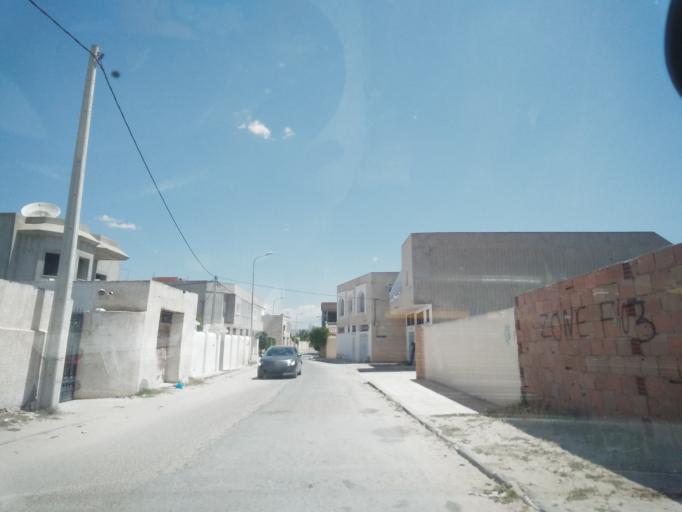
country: TN
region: Safaqis
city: Al Qarmadah
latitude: 34.8230
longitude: 10.7688
